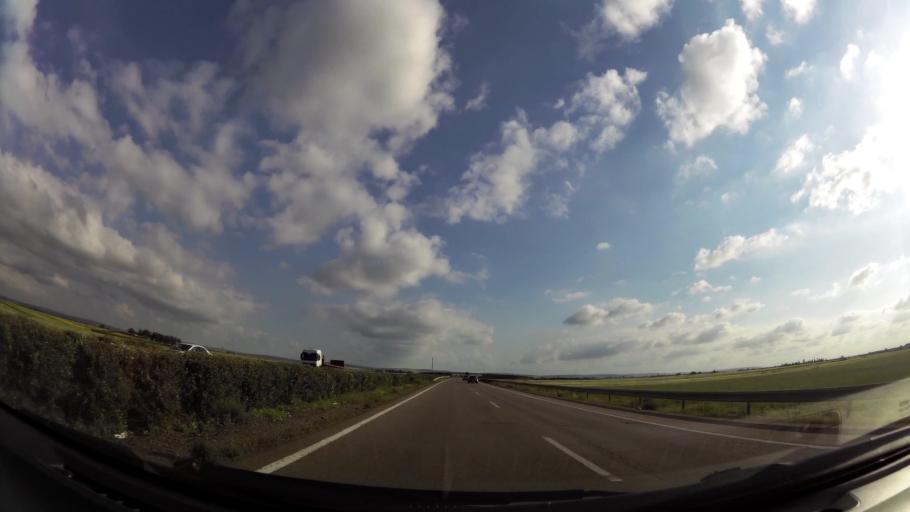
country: MA
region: Chaouia-Ouardigha
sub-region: Settat Province
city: Berrechid
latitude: 33.1537
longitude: -7.5716
